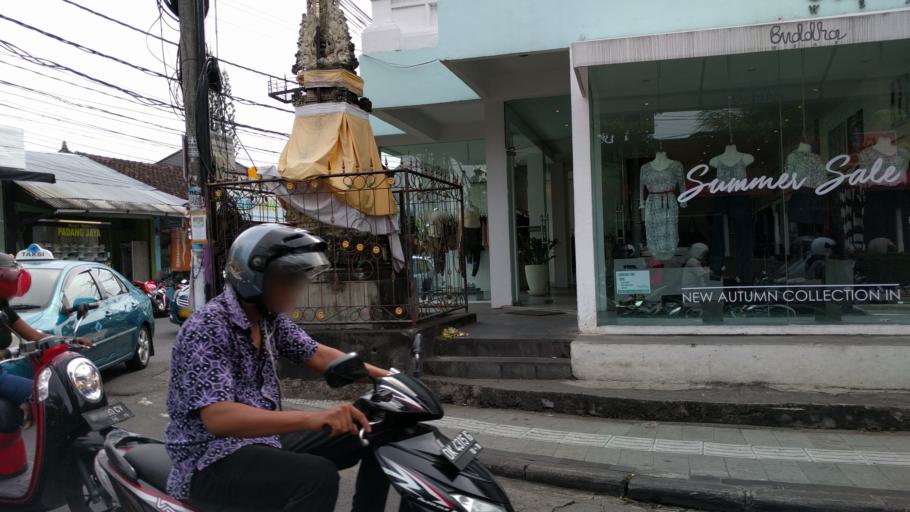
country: ID
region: Bali
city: Kuta
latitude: -8.6909
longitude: 115.1677
